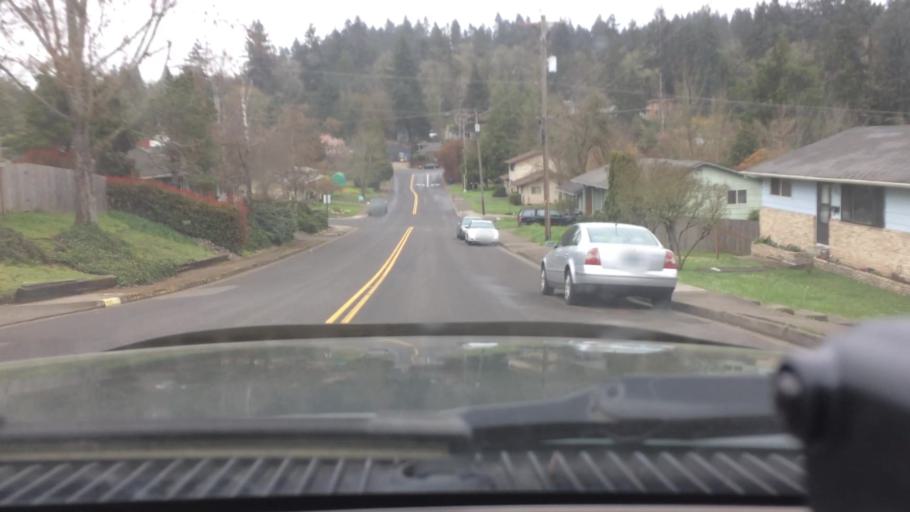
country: US
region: Oregon
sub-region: Lane County
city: Eugene
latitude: 44.0290
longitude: -123.1013
